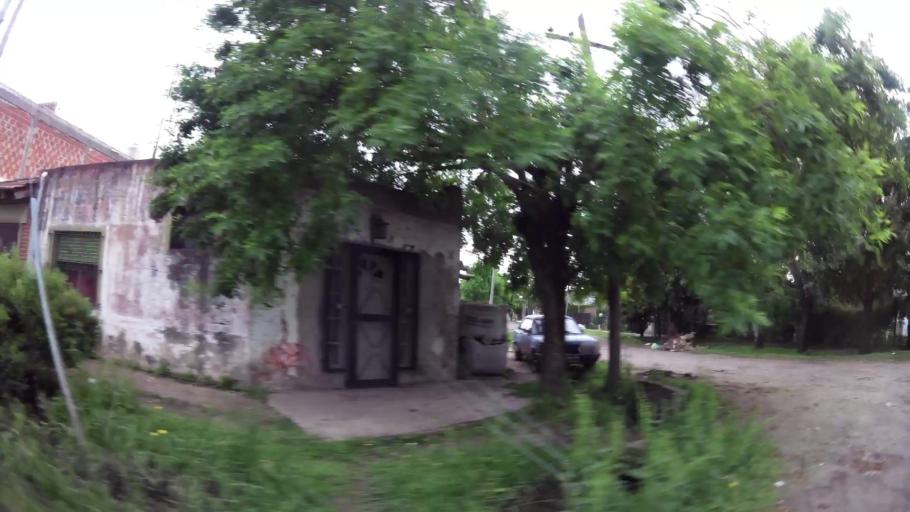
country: AR
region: Buenos Aires
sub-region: Partido de Quilmes
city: Quilmes
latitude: -34.7957
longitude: -58.2695
